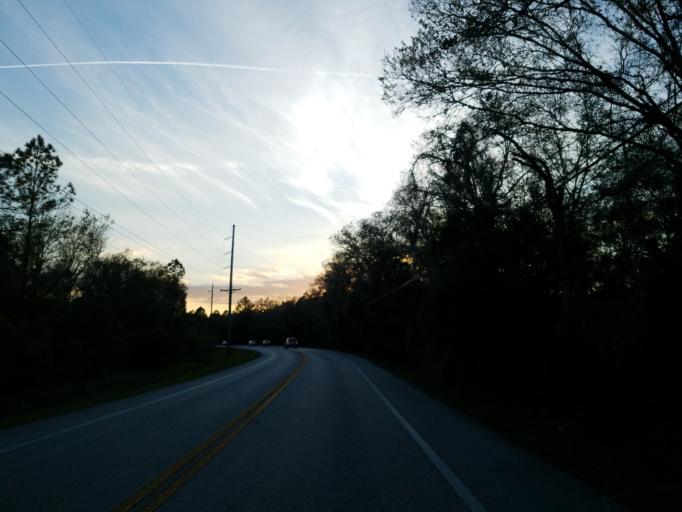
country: US
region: Florida
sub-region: Hillsborough County
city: Thonotosassa
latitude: 28.0962
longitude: -82.3167
